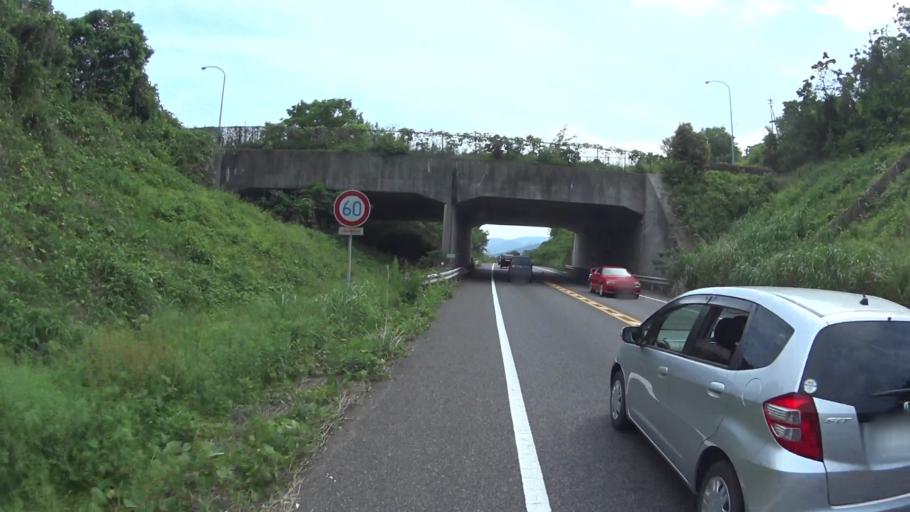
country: JP
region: Shiga Prefecture
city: Kitahama
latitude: 35.0908
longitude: 135.8888
